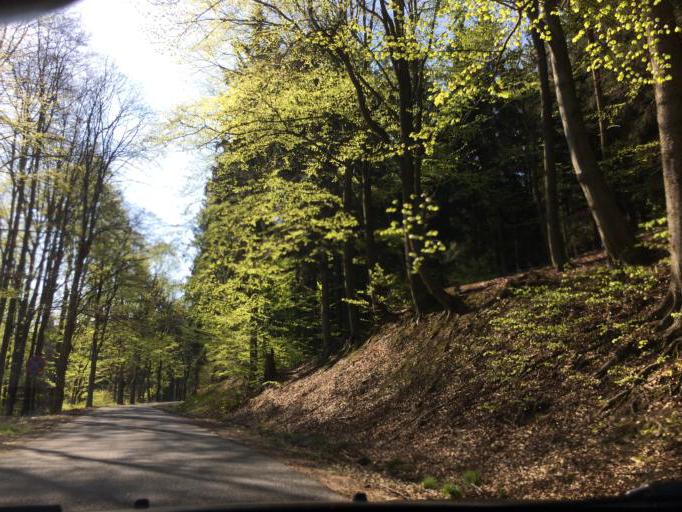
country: PL
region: Lower Silesian Voivodeship
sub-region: Powiat klodzki
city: Jugow
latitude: 50.6698
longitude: 16.5161
